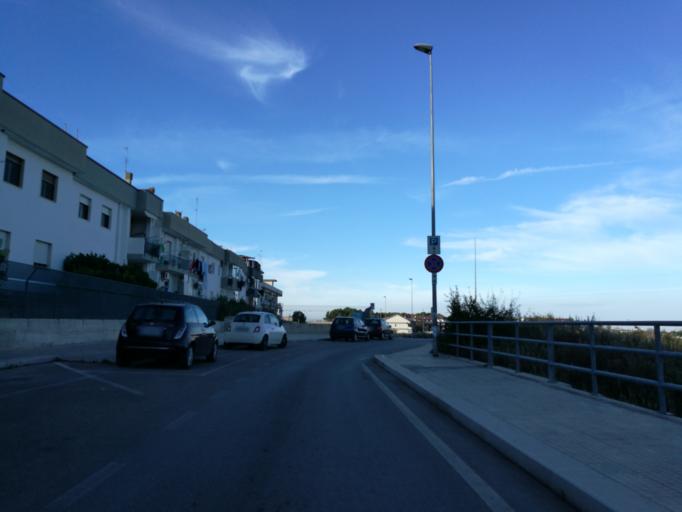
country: IT
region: Apulia
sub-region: Provincia di Bari
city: Adelfia
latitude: 41.0045
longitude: 16.8721
